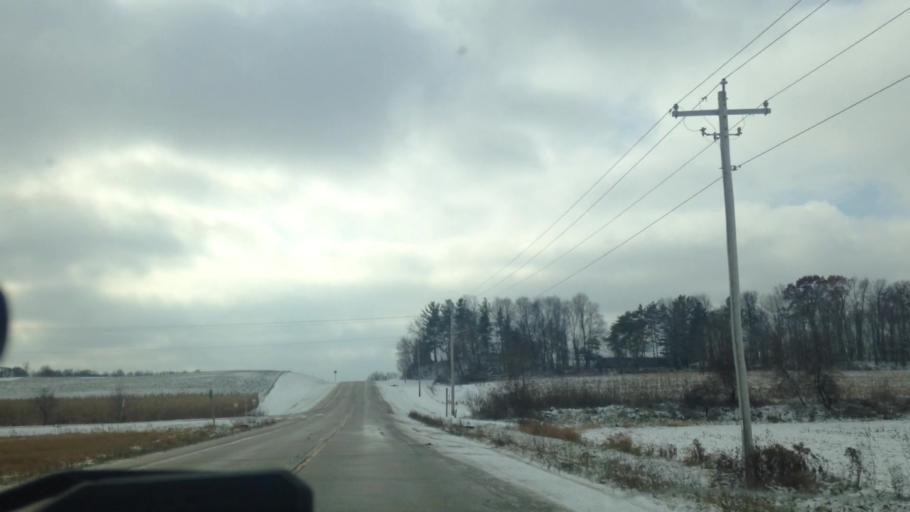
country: US
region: Wisconsin
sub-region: Dodge County
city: Mayville
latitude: 43.4545
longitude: -88.4999
